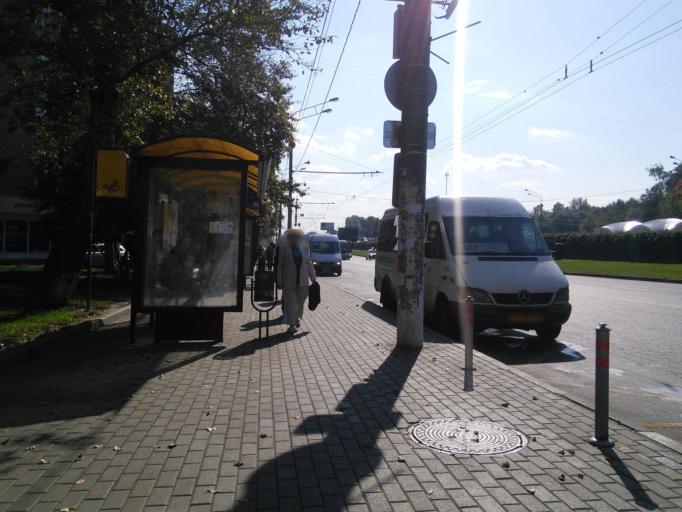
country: RU
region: Moscow
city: Tsaritsyno
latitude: 55.6361
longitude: 37.6569
